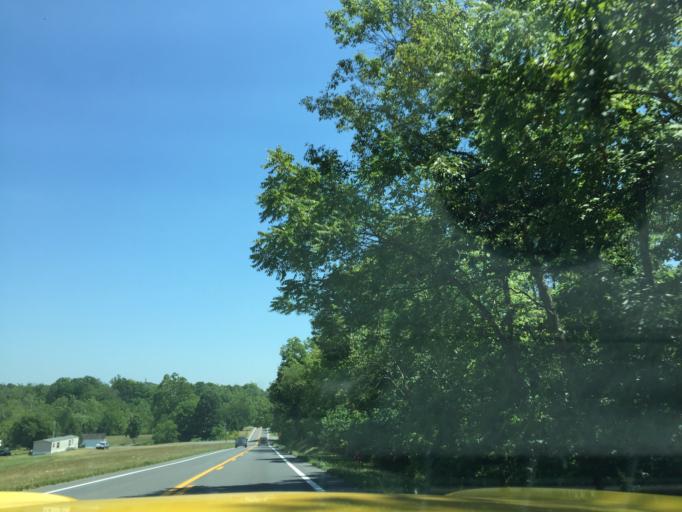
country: US
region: West Virginia
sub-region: Berkeley County
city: Inwood
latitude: 39.3217
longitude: -77.9929
